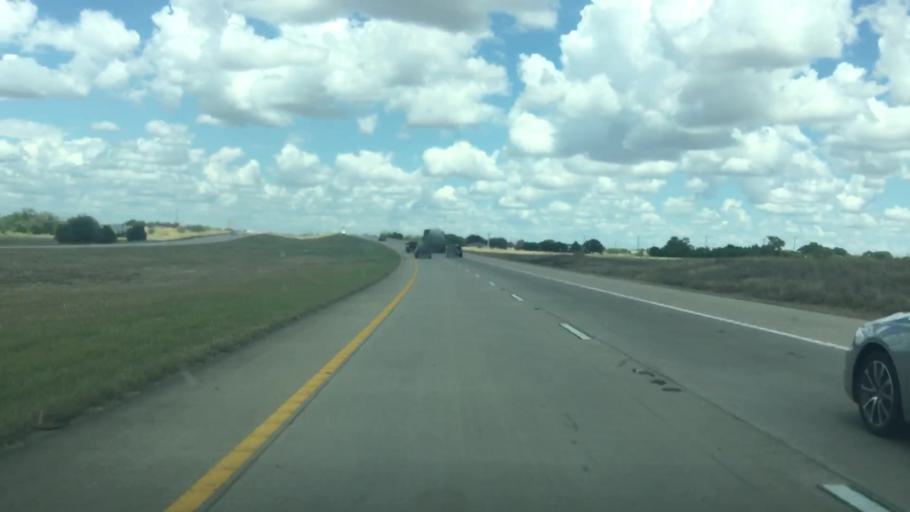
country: US
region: Texas
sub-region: Williamson County
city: Hutto
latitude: 30.5567
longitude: -97.5769
